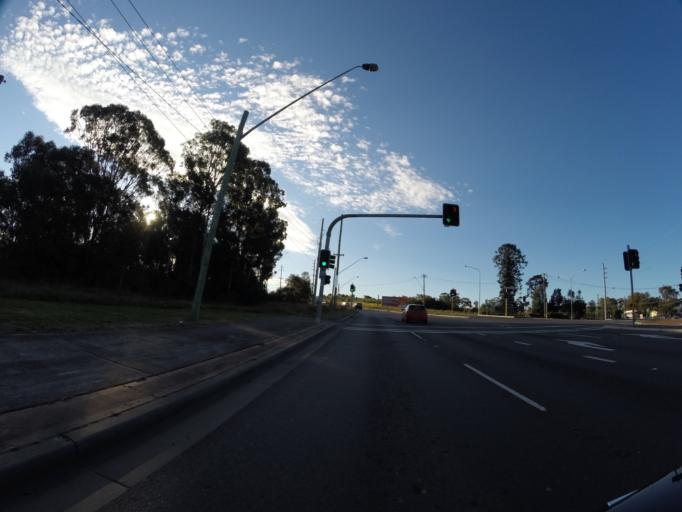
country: AU
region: New South Wales
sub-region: Fairfield
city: Horsley Park
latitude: -33.8495
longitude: 150.8763
